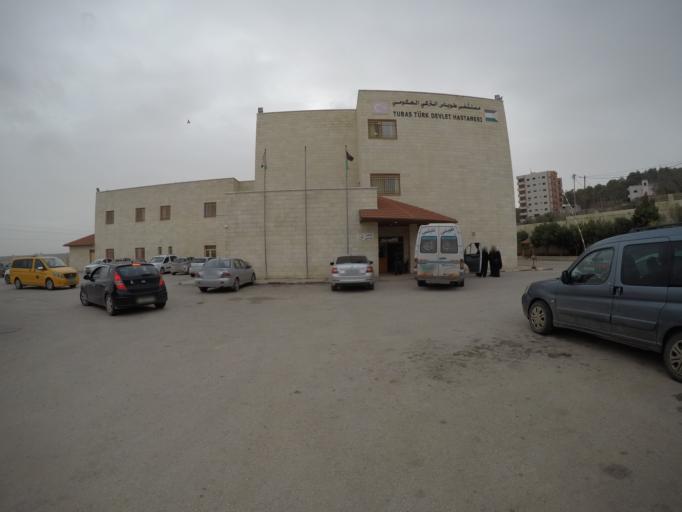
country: PS
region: West Bank
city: Tubas
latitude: 32.3365
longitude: 35.3581
